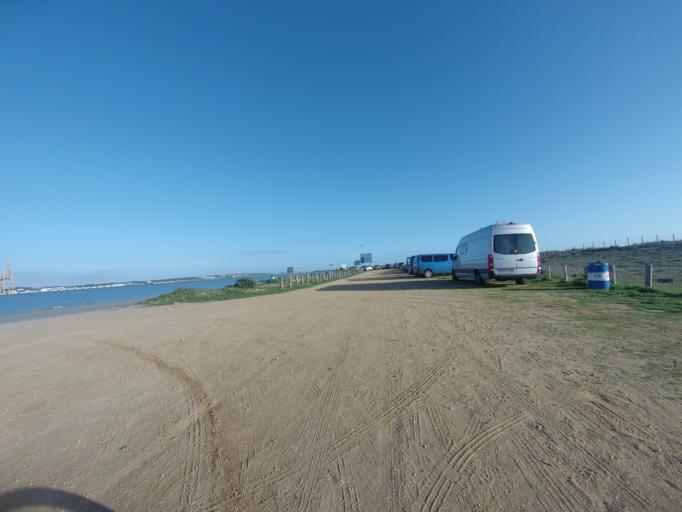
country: ES
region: Andalusia
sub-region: Provincia de Huelva
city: Punta Umbria
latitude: 37.1465
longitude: -6.8905
